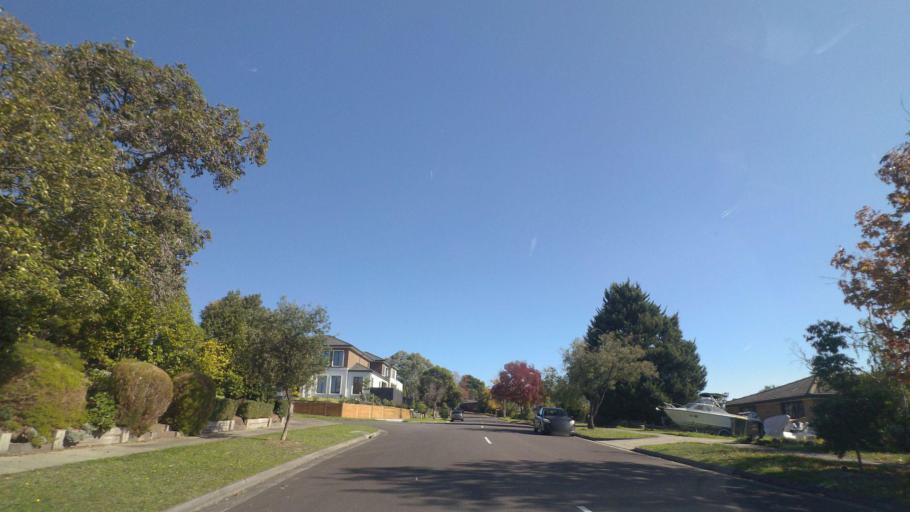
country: AU
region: Victoria
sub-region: Nillumbik
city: Eltham
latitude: -37.7537
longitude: 145.1618
